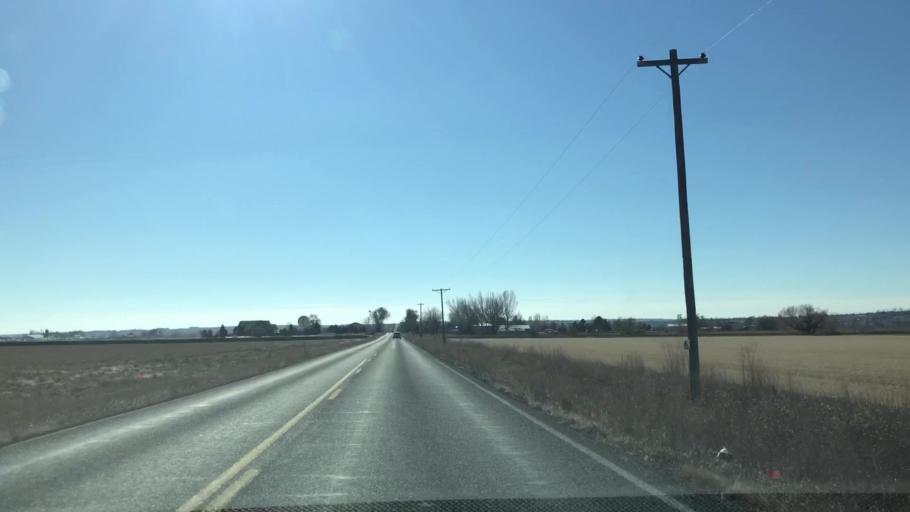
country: US
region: Colorado
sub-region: Weld County
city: Windsor
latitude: 40.5036
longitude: -104.9442
